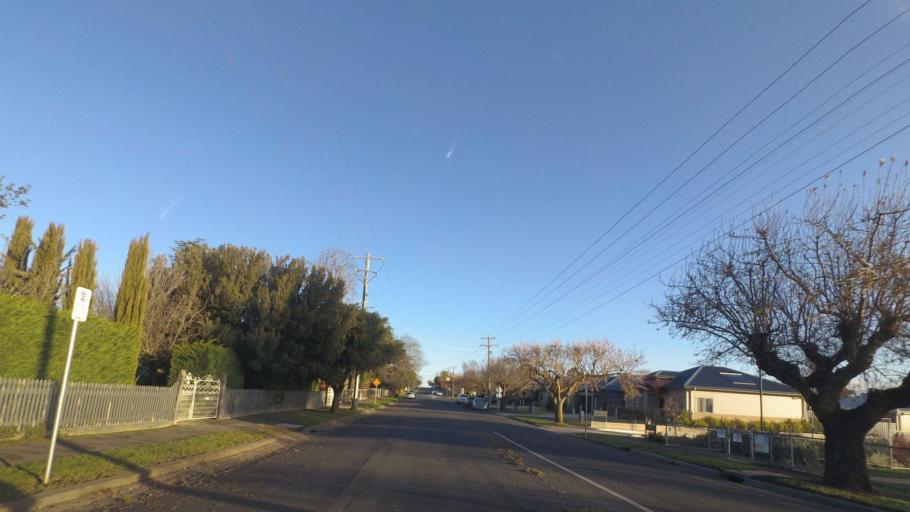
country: AU
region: Victoria
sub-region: Mount Alexander
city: Castlemaine
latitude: -37.2507
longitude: 144.4625
